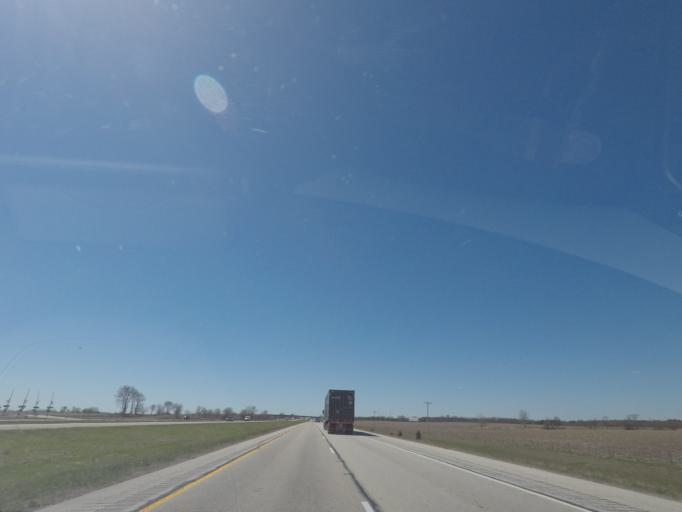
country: US
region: Illinois
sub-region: McLean County
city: Lexington
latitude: 40.6106
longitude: -88.8313
